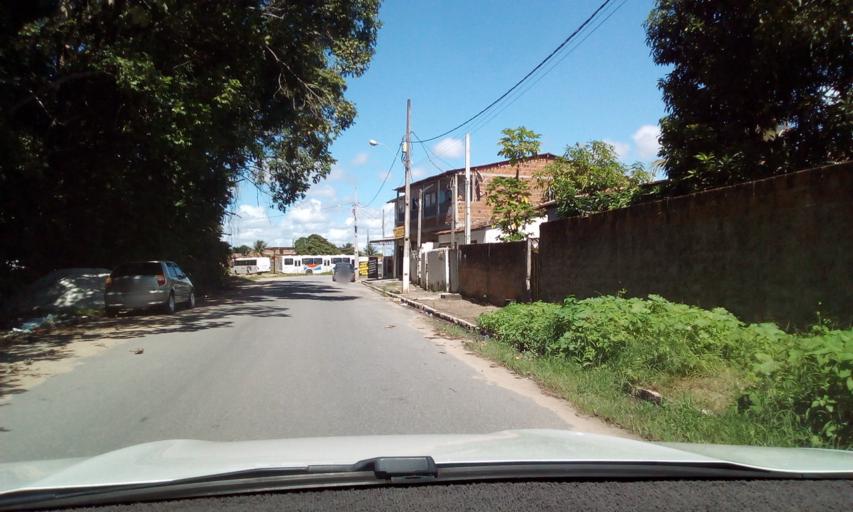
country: BR
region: Paraiba
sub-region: Joao Pessoa
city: Joao Pessoa
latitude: -7.1811
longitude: -34.8240
